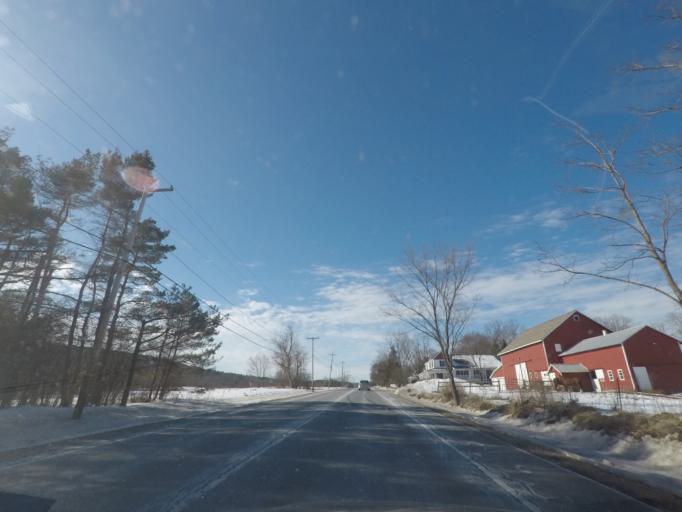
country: US
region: New York
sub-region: Albany County
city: Altamont
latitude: 42.7406
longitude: -74.0179
